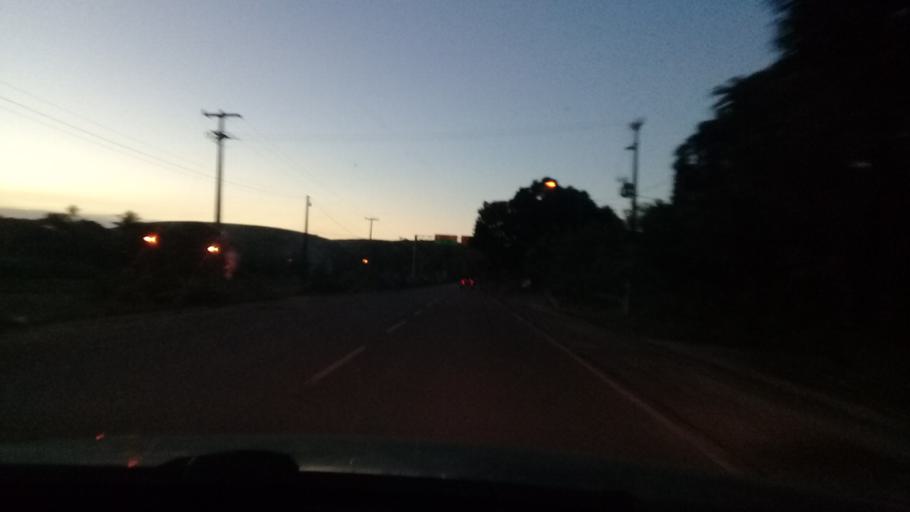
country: BR
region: Pernambuco
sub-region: Sirinhaem
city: Sirinhaem
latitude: -8.5119
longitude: -35.0949
